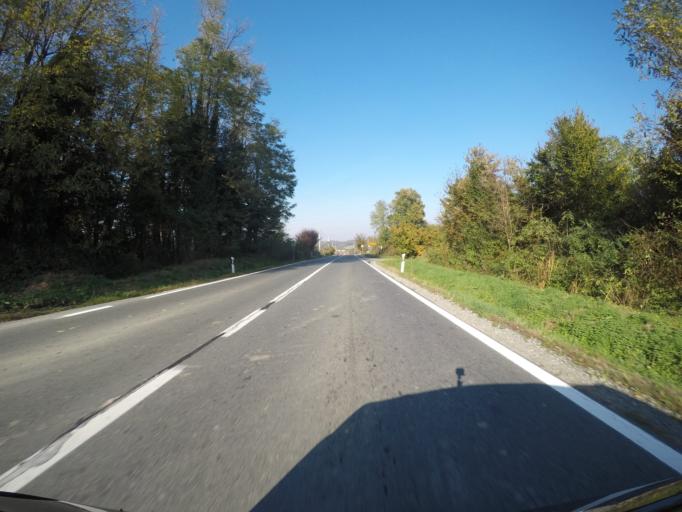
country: HR
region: Bjelovarsko-Bilogorska
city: Bjelovar
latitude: 45.9629
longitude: 16.8921
